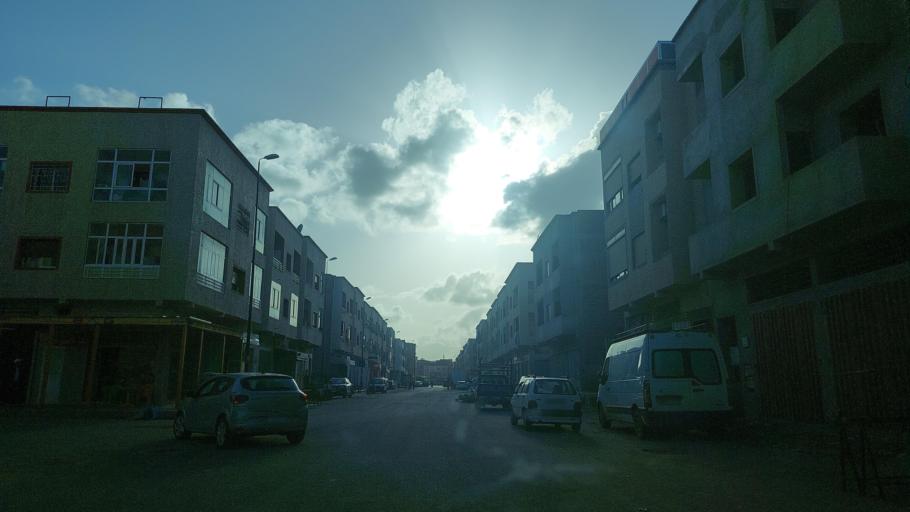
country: MA
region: Grand Casablanca
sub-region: Mediouna
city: Mediouna
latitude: 33.3768
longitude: -7.5307
